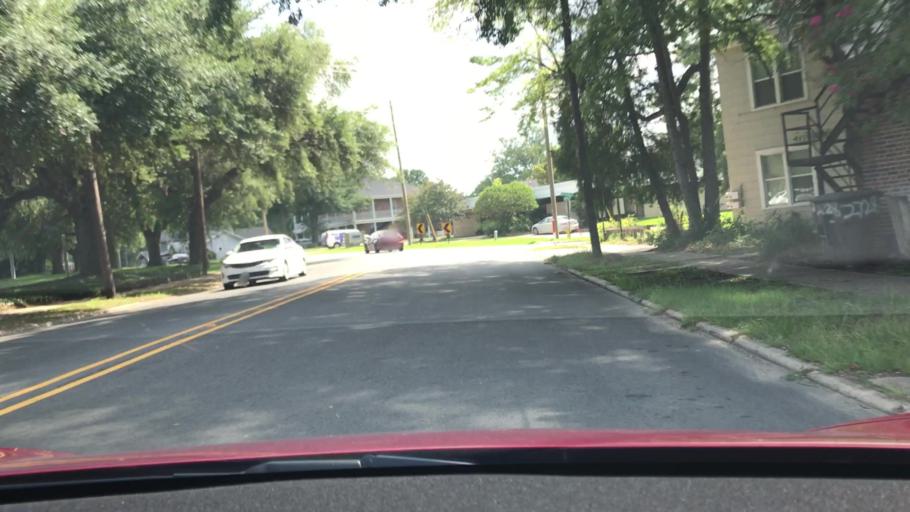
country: US
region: Louisiana
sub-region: Bossier Parish
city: Bossier City
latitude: 32.4852
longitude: -93.7336
